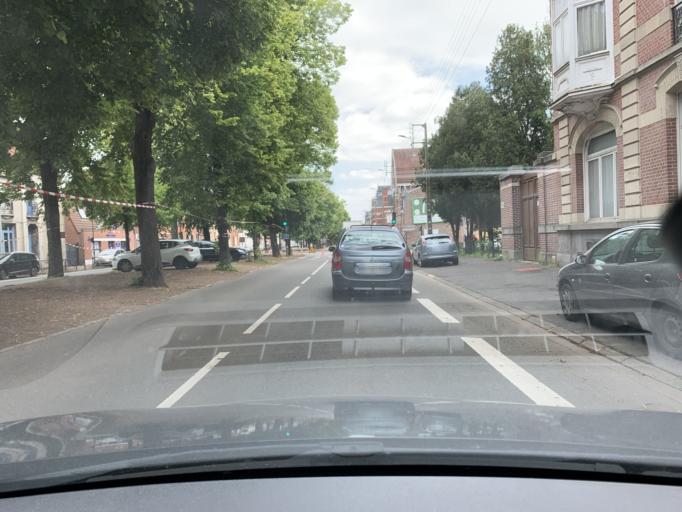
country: FR
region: Nord-Pas-de-Calais
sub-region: Departement du Nord
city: Douai
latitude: 50.3638
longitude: 3.0747
